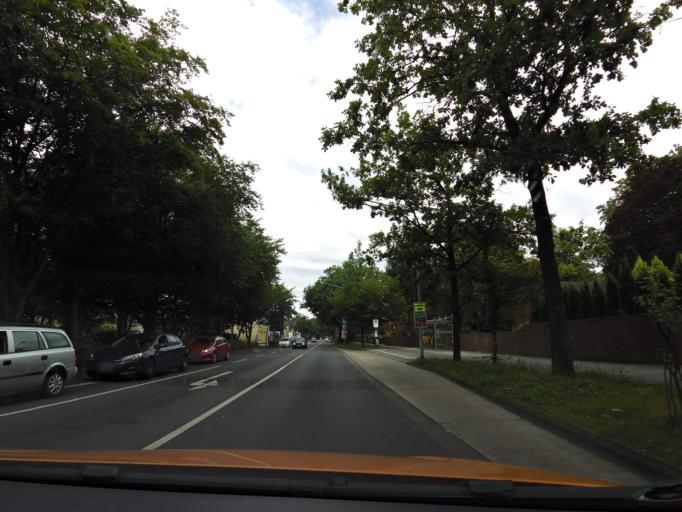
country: DE
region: Lower Saxony
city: Oldenburg
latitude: 53.1450
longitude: 8.1898
